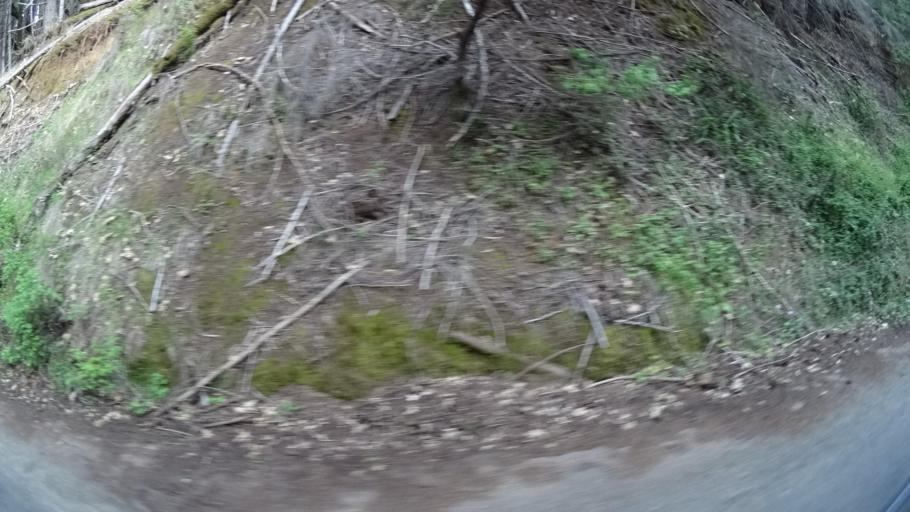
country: US
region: California
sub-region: Humboldt County
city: Redway
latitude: 40.2115
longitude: -123.6680
